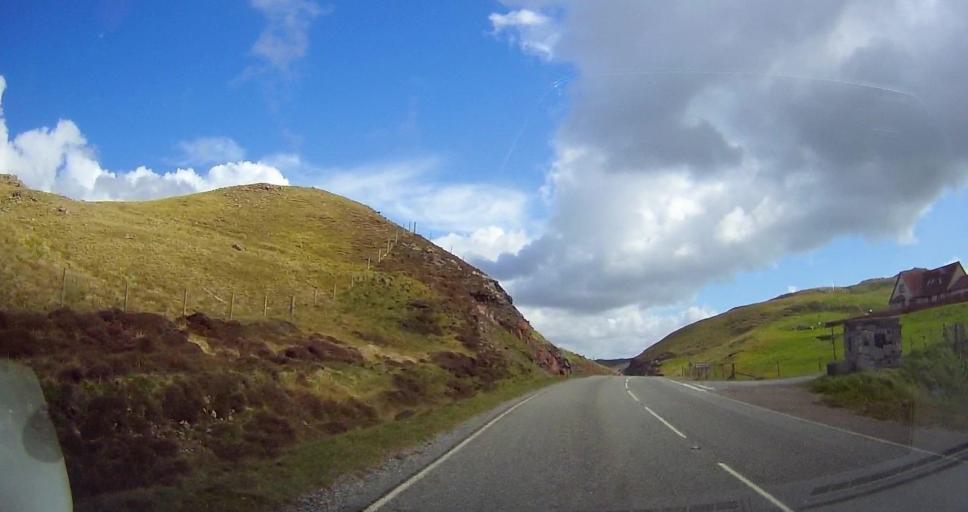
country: GB
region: Scotland
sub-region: Shetland Islands
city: Lerwick
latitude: 60.4062
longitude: -1.3865
